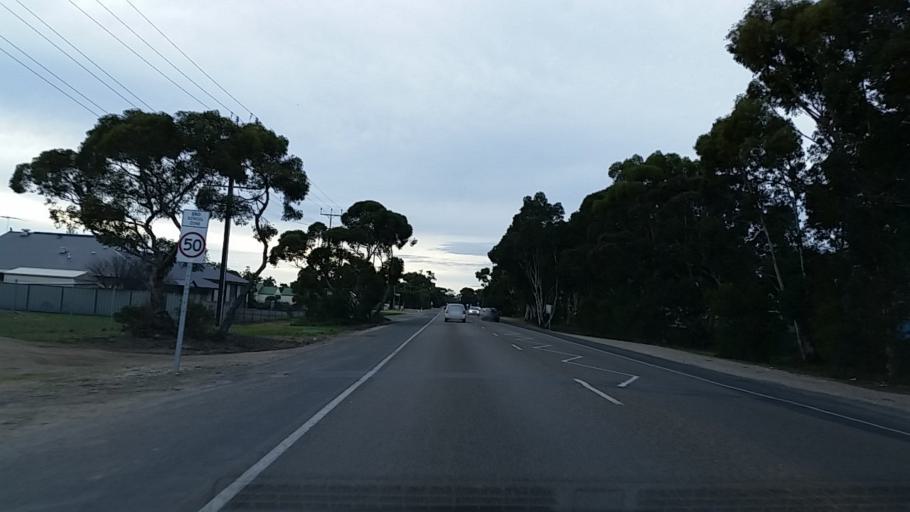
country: AU
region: South Australia
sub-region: Murray Bridge
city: Murray Bridge
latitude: -35.1453
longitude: 139.2859
